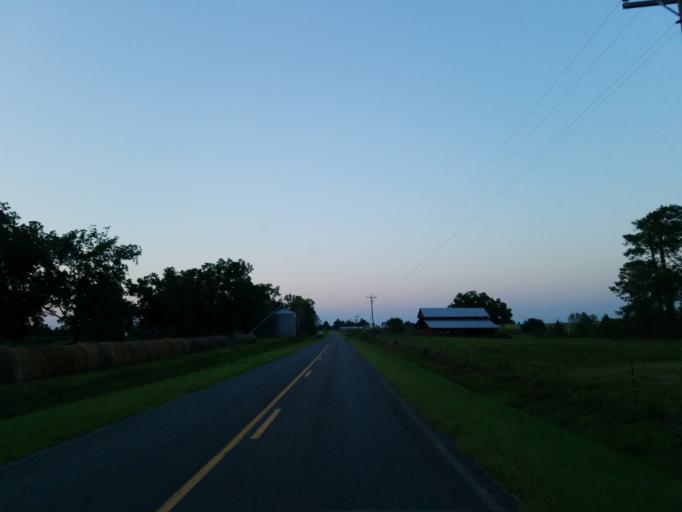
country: US
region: Georgia
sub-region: Dooly County
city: Vienna
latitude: 32.1823
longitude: -83.7979
